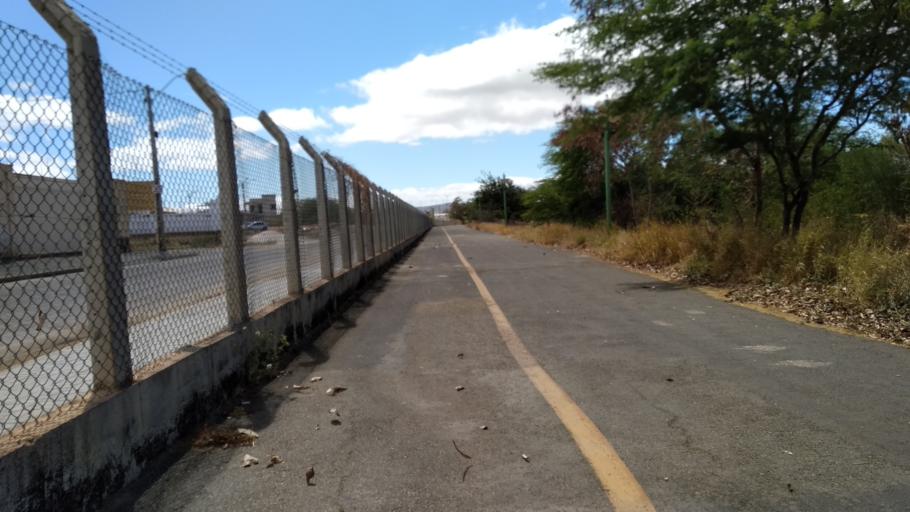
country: BR
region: Bahia
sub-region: Guanambi
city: Guanambi
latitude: -14.2258
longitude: -42.7667
